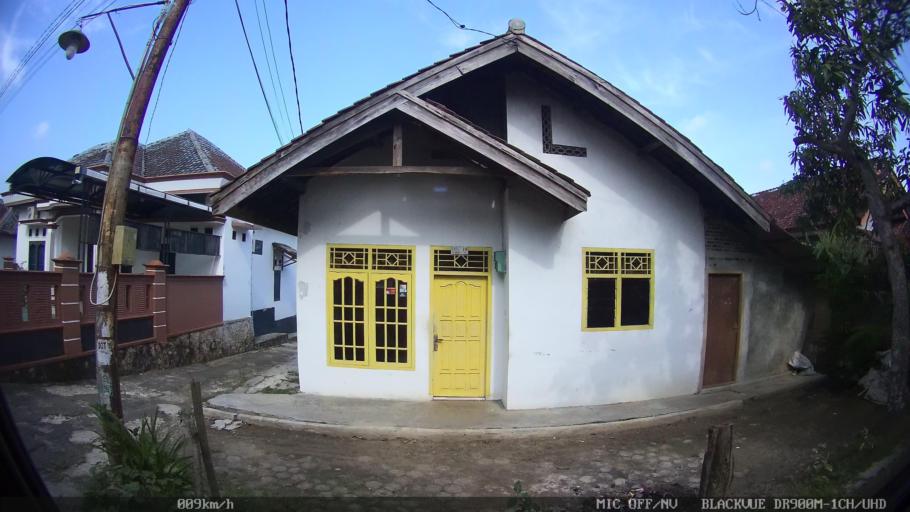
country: ID
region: Lampung
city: Kedaton
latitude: -5.3881
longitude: 105.2213
